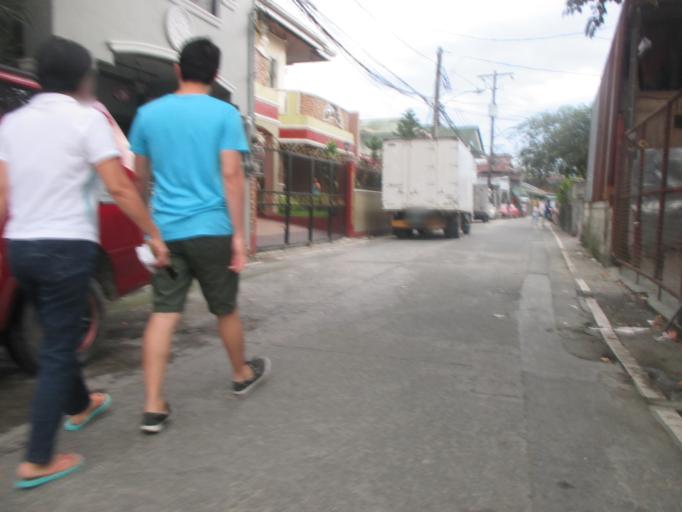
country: PH
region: Metro Manila
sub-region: Marikina
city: Calumpang
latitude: 14.6241
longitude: 121.0900
